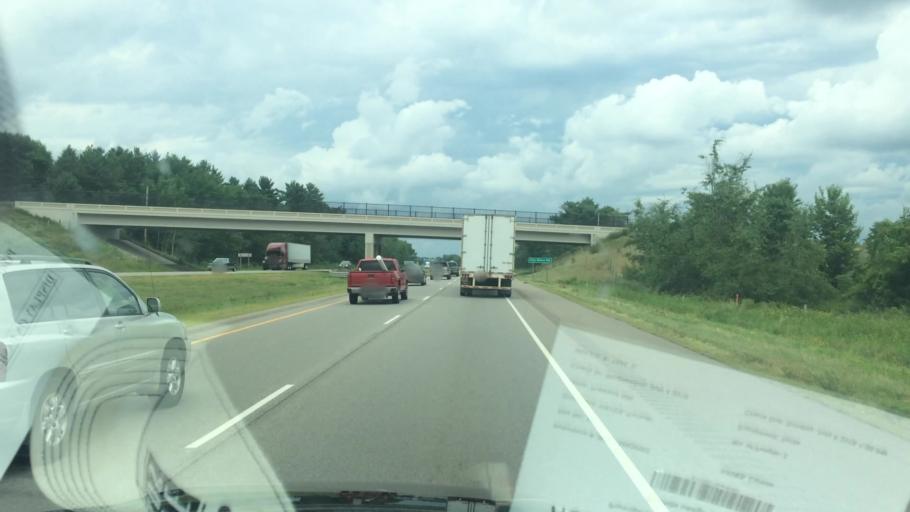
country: US
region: Wisconsin
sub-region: Marathon County
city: Rothschild
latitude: 44.8789
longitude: -89.6427
